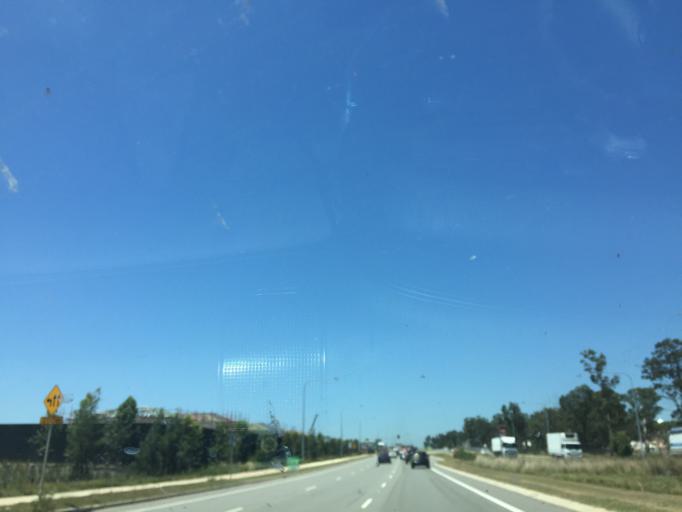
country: AU
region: New South Wales
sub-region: Blacktown
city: Hassall Grove
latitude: -33.7215
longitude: 150.8444
